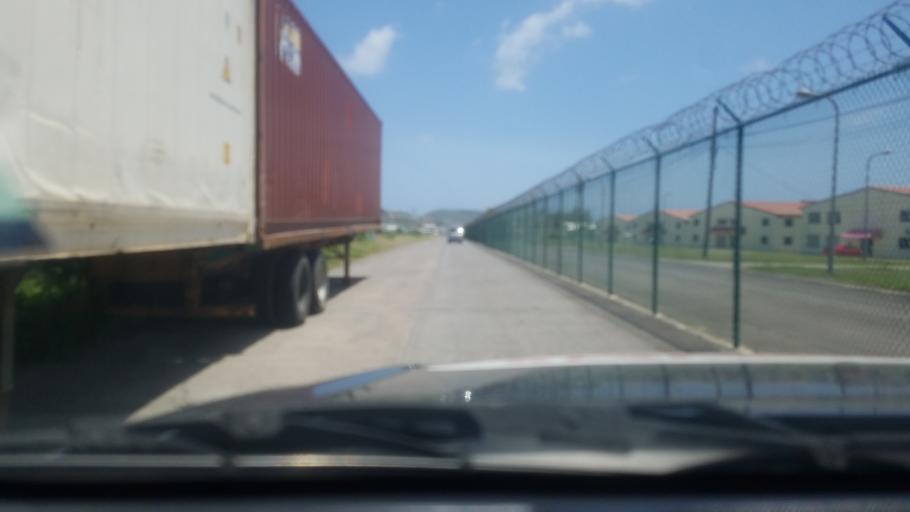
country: LC
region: Vieux-Fort
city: Vieux Fort
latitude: 13.7415
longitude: -60.9478
